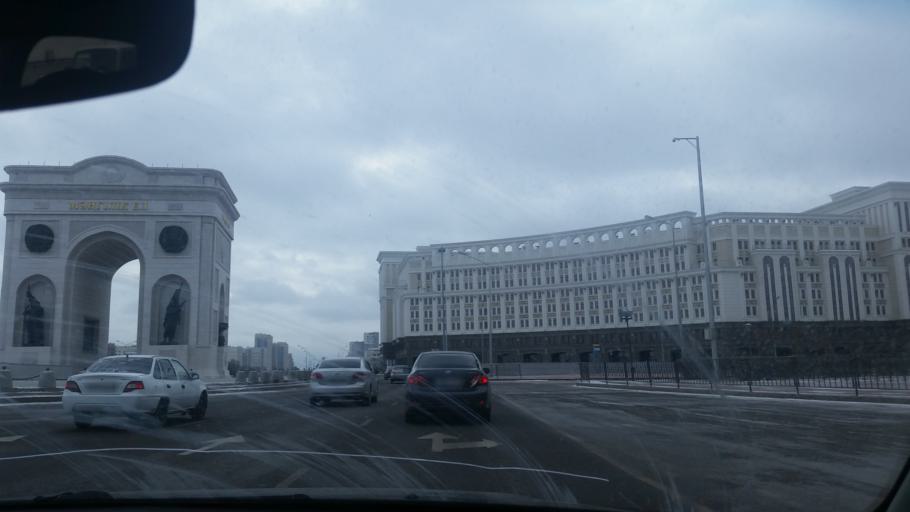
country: KZ
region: Astana Qalasy
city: Astana
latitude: 51.1051
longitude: 71.4300
